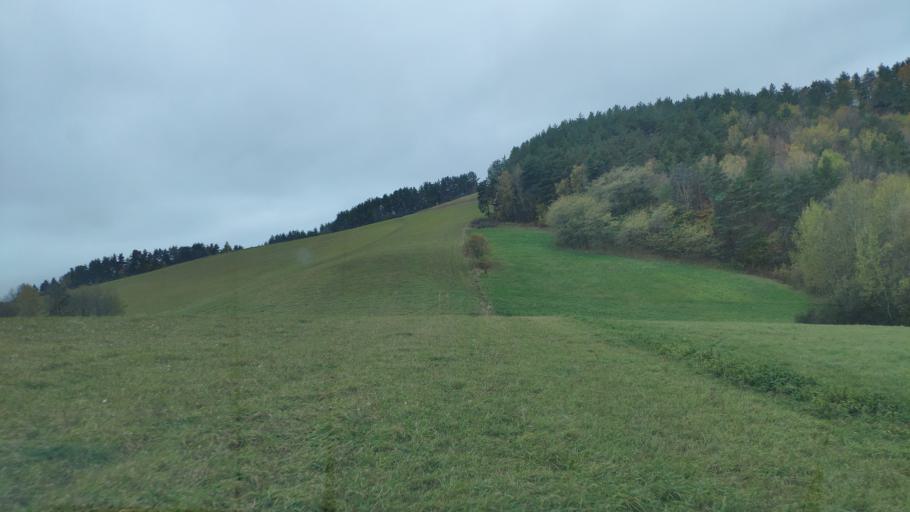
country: SK
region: Presovsky
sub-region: Okres Presov
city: Presov
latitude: 48.9357
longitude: 21.1147
